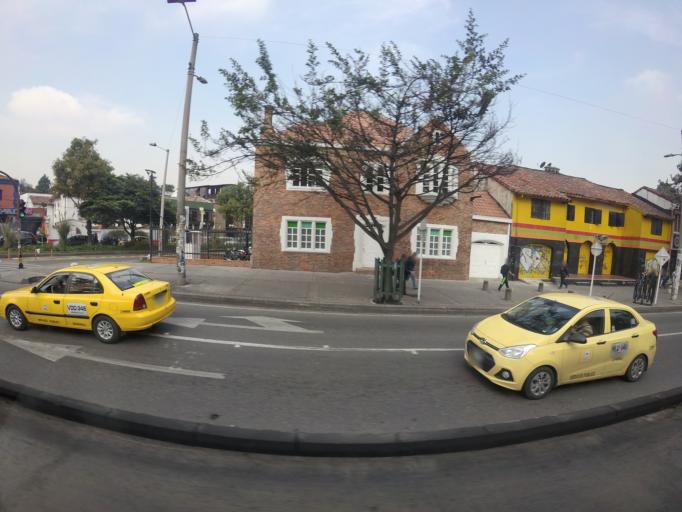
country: CO
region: Bogota D.C.
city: Bogota
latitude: 4.6283
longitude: -74.0685
